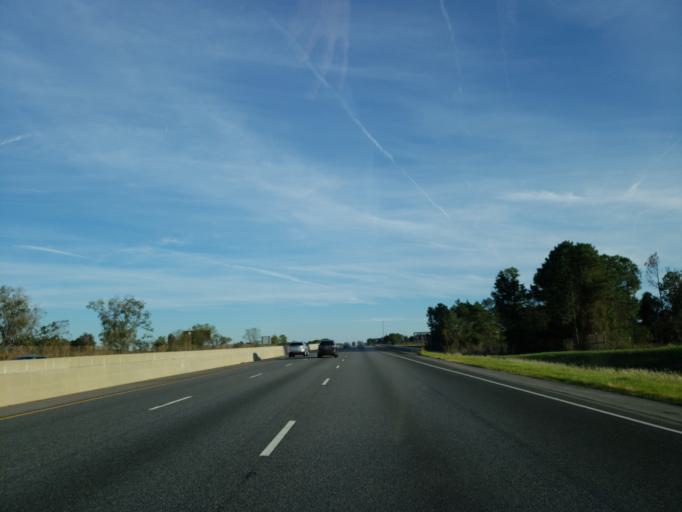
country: US
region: Georgia
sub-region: Turner County
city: Ashburn
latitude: 31.6620
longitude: -83.6049
